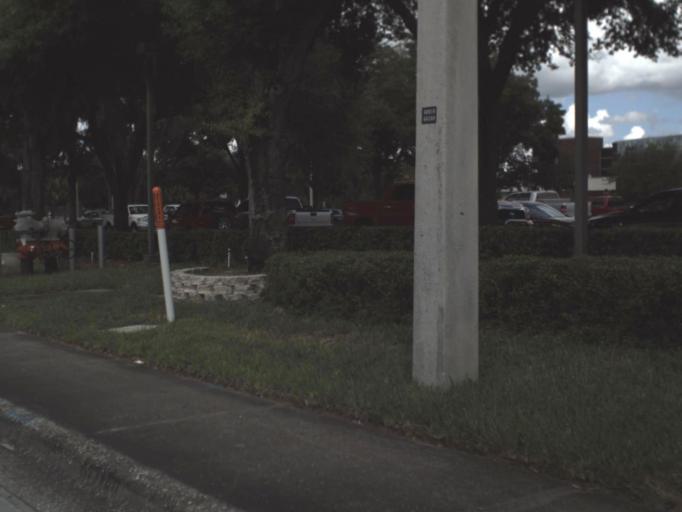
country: US
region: Florida
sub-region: Polk County
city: Winter Haven
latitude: 28.0279
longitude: -81.7268
